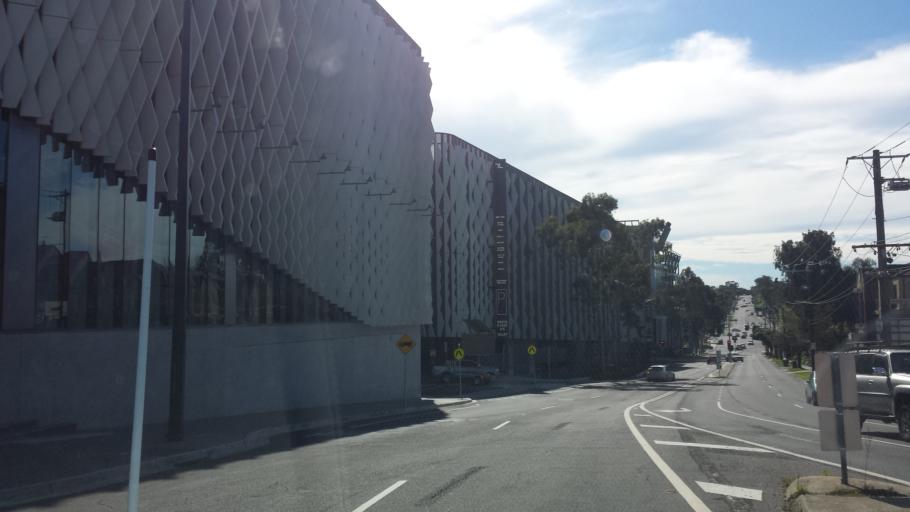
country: AU
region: Victoria
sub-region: Maroondah
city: Ringwood East
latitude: -37.8145
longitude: 145.2310
